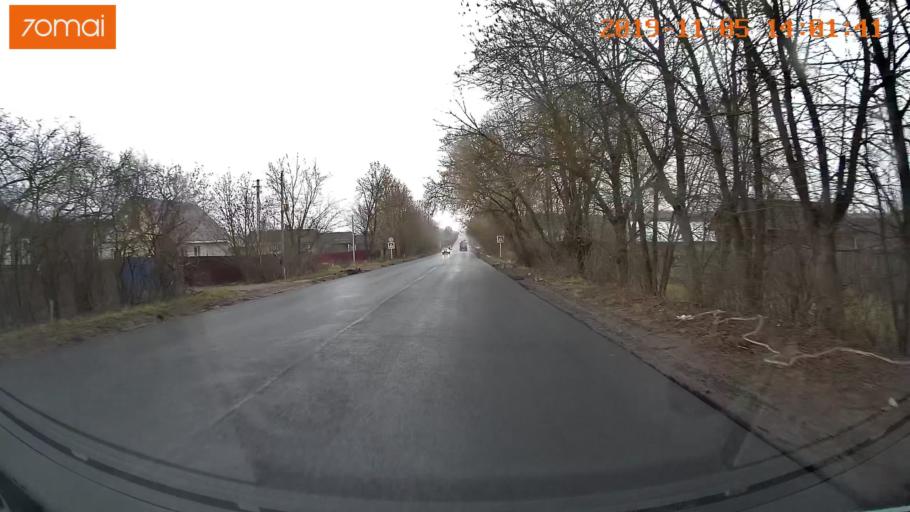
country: RU
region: Ivanovo
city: Kitovo
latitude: 57.0073
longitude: 41.2261
